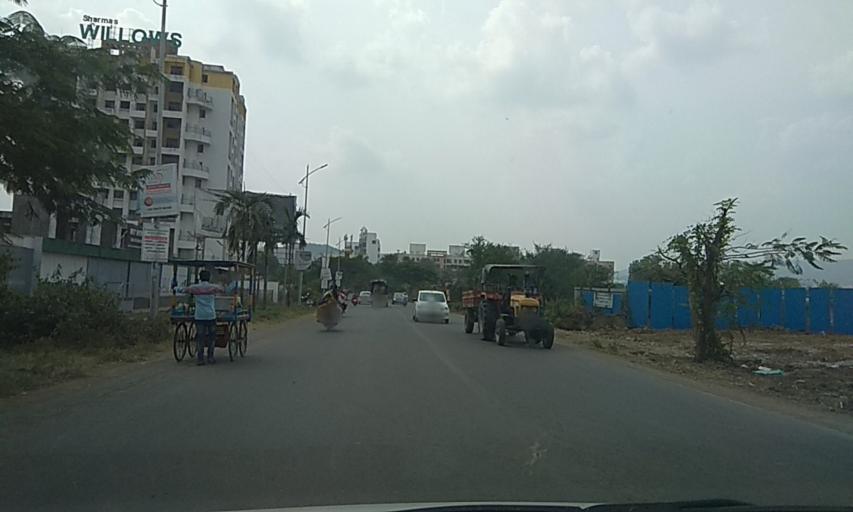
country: IN
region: Maharashtra
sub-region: Pune Division
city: Pimpri
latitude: 18.5777
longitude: 73.7140
